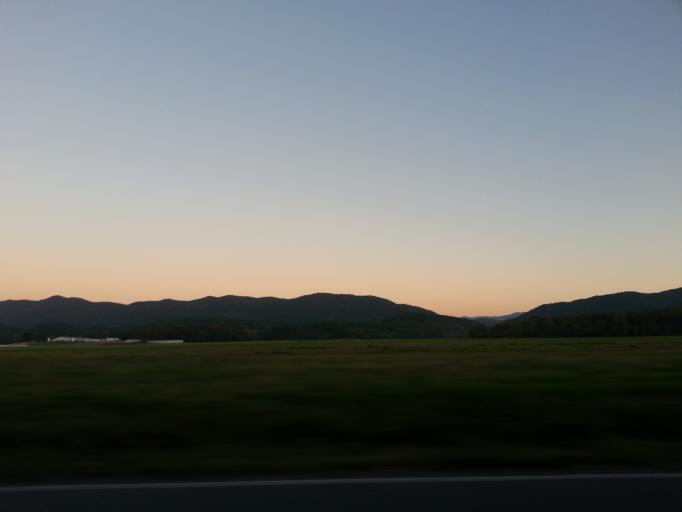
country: US
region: Tennessee
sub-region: Blount County
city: Wildwood
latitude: 35.7684
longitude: -83.8541
